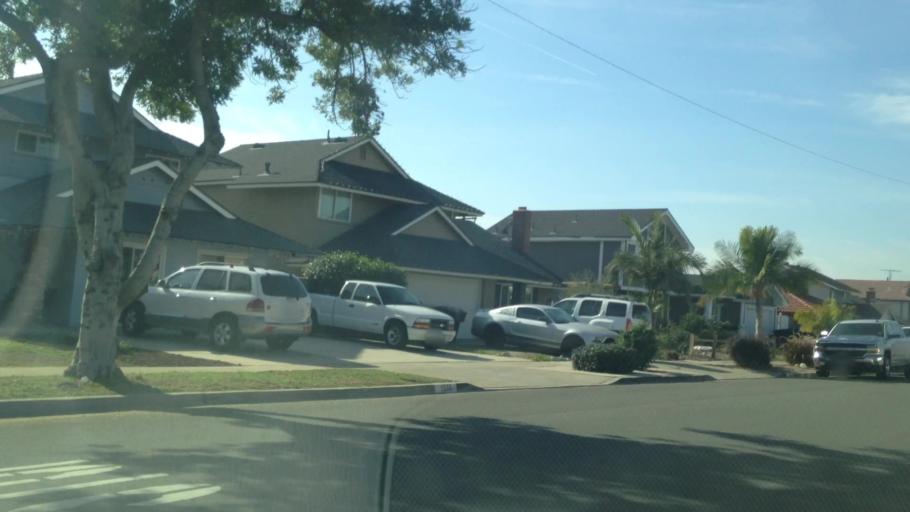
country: US
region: California
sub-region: Orange County
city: Yorba Linda
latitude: 33.8841
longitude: -117.8373
